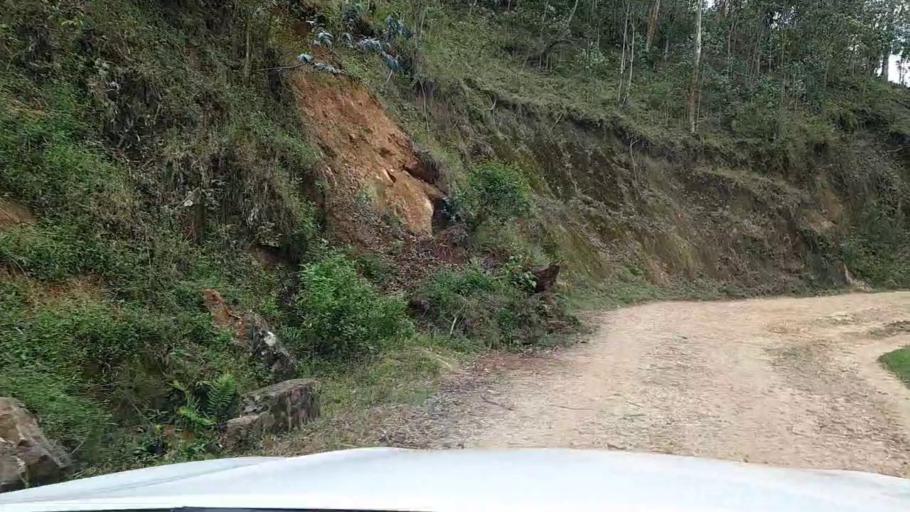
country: RW
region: Western Province
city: Kibuye
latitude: -2.2711
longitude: 29.3637
